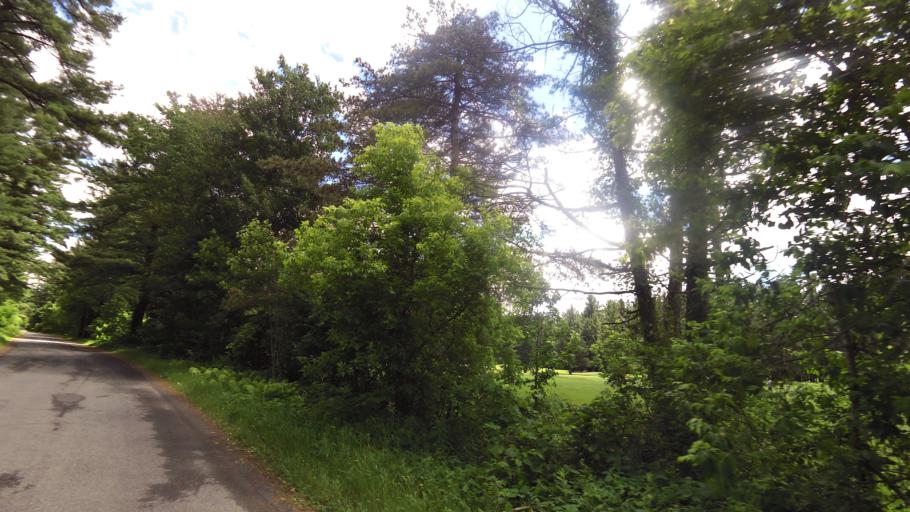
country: CA
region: Quebec
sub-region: Laurentides
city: Oka
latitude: 45.4684
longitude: -74.0947
